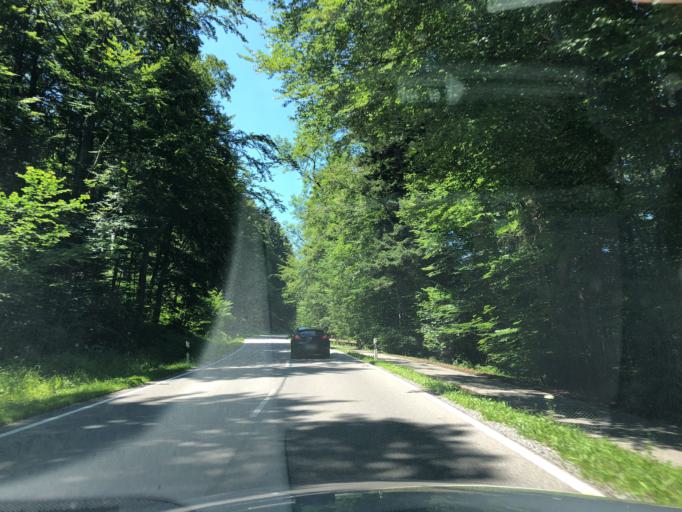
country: DE
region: Bavaria
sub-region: Upper Bavaria
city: Aschau im Chiemgau
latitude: 47.7922
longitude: 12.3077
